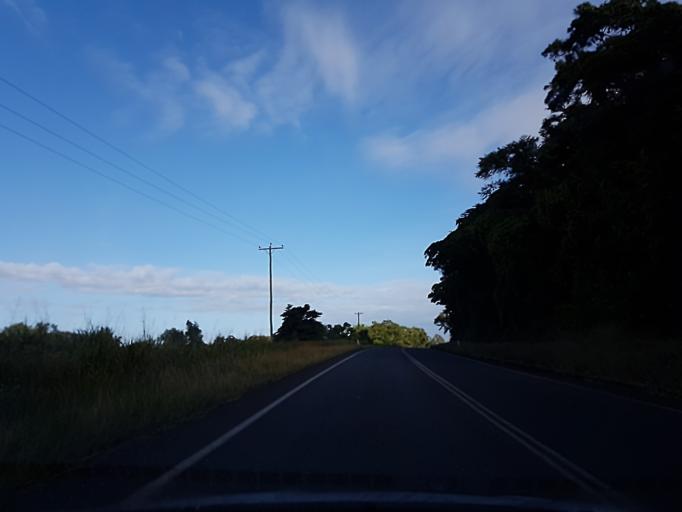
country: AU
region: Queensland
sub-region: Cairns
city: Port Douglas
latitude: -16.3218
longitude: 145.4073
